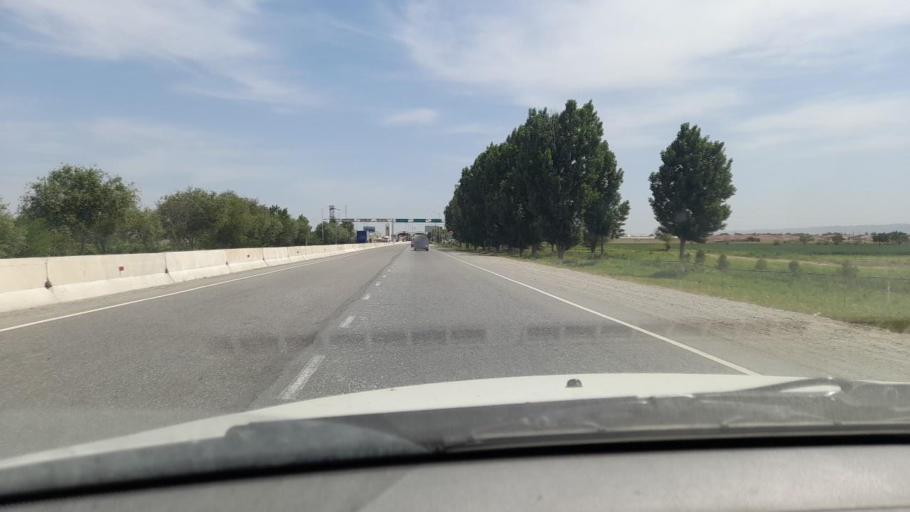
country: UZ
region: Navoiy
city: Karmana Shahri
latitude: 40.1205
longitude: 65.4837
